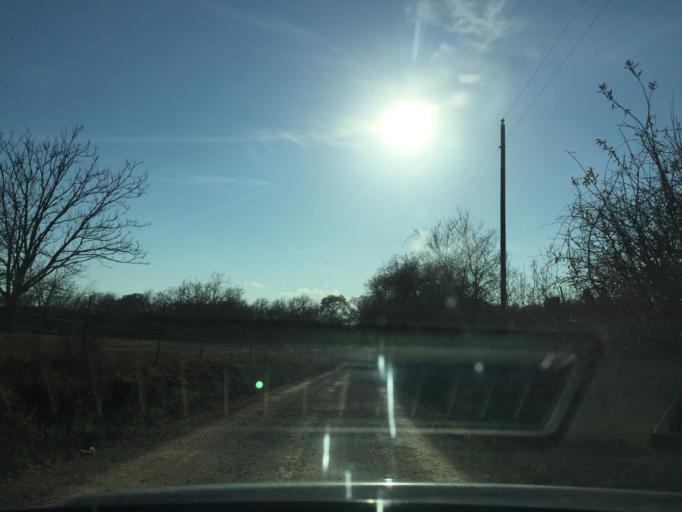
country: US
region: Texas
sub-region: Bastrop County
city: Elgin
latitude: 30.4145
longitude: -97.2197
